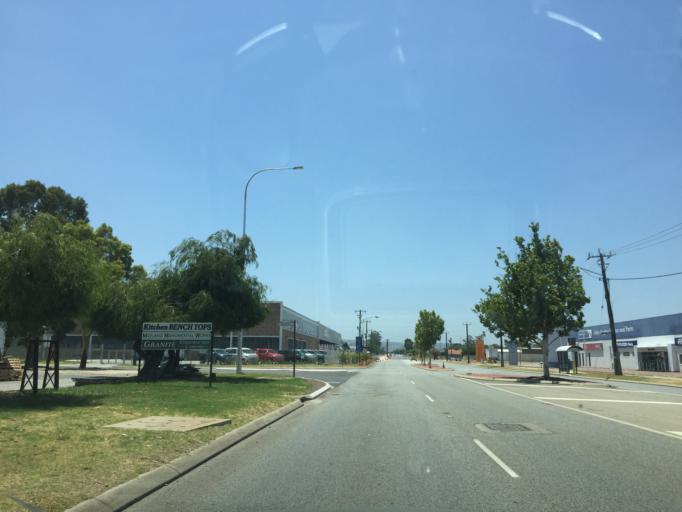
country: AU
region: Western Australia
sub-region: Canning
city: Queens Park
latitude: -31.9954
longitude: 115.9365
